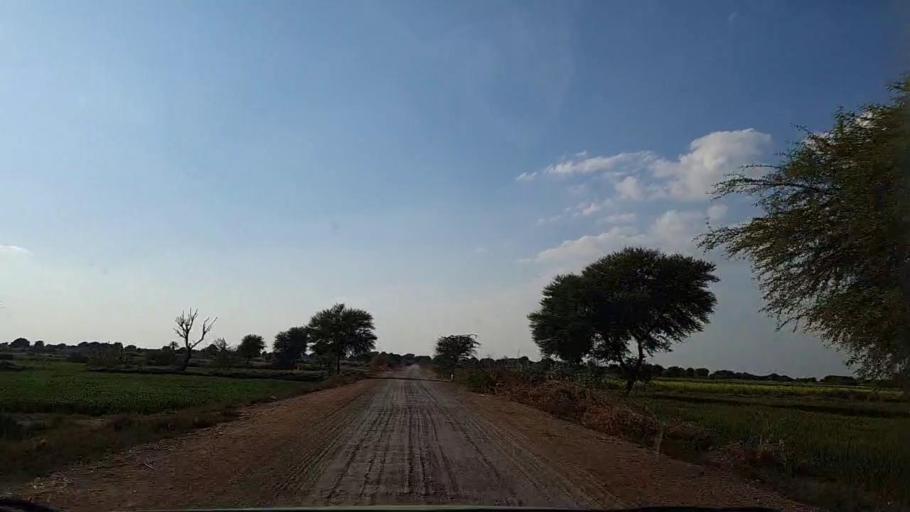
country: PK
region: Sindh
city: Pithoro
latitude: 25.6495
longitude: 69.2920
